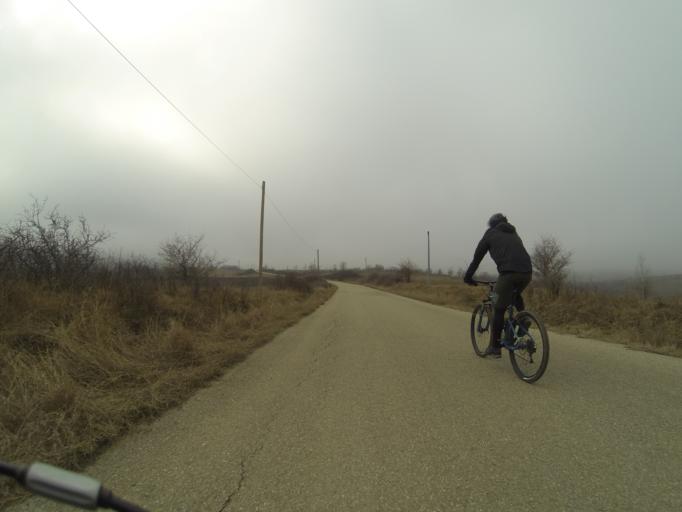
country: RO
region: Mehedinti
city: Dumbrava de Sus
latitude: 44.4912
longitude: 23.0840
